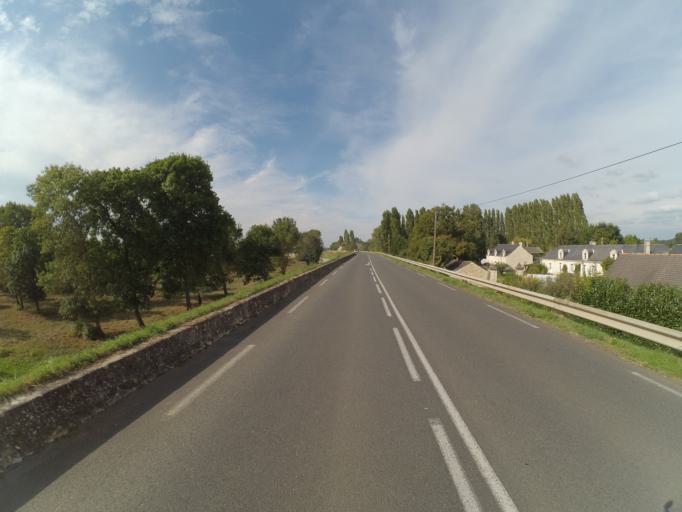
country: FR
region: Pays de la Loire
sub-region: Departement de Maine-et-Loire
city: Varennes-sur-Loire
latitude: 47.2377
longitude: 0.0227
